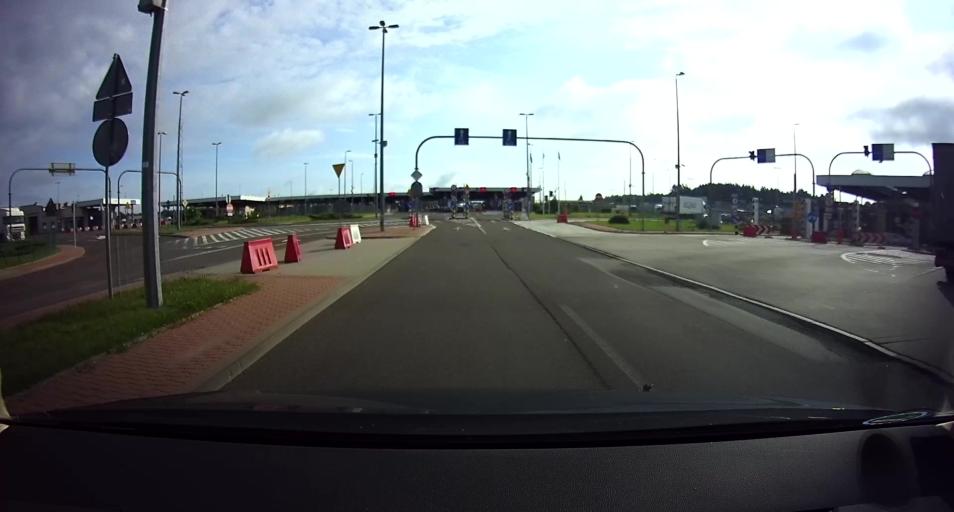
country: PL
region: Podlasie
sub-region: Powiat sokolski
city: Kuznica
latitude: 53.5196
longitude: 23.6554
